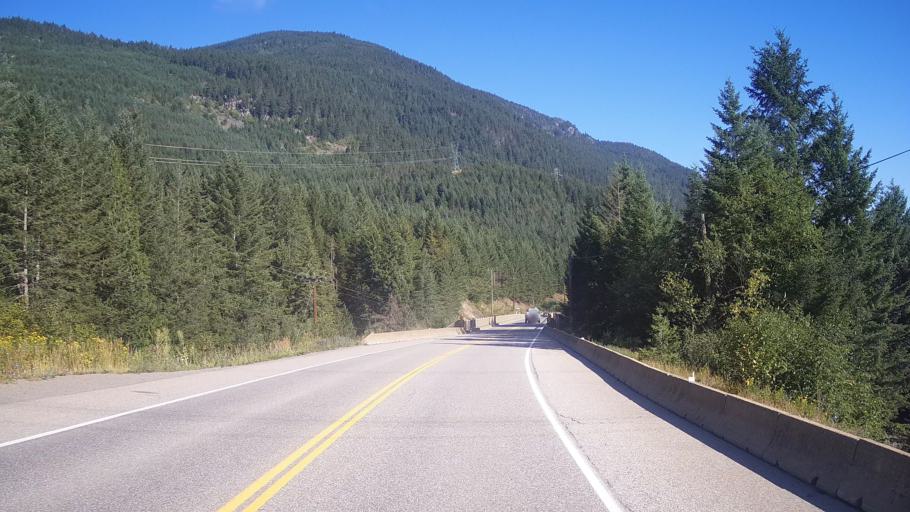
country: CA
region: British Columbia
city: Hope
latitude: 49.6640
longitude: -121.4184
